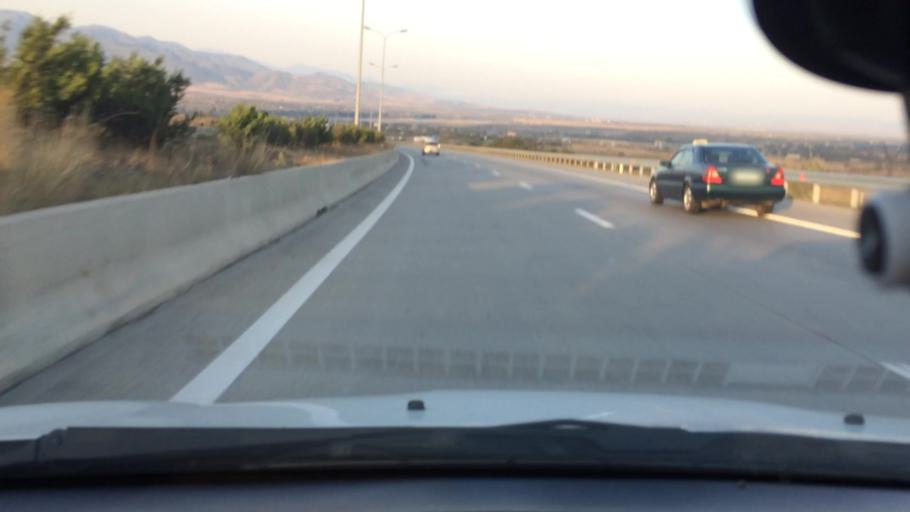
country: GE
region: Shida Kartli
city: Gori
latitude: 42.0203
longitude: 44.0029
